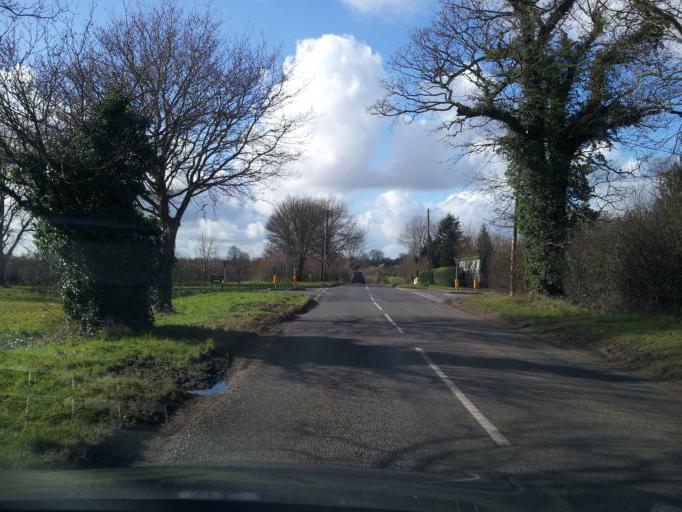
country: GB
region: England
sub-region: Norfolk
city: Mattishall
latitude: 52.6579
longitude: 1.0989
